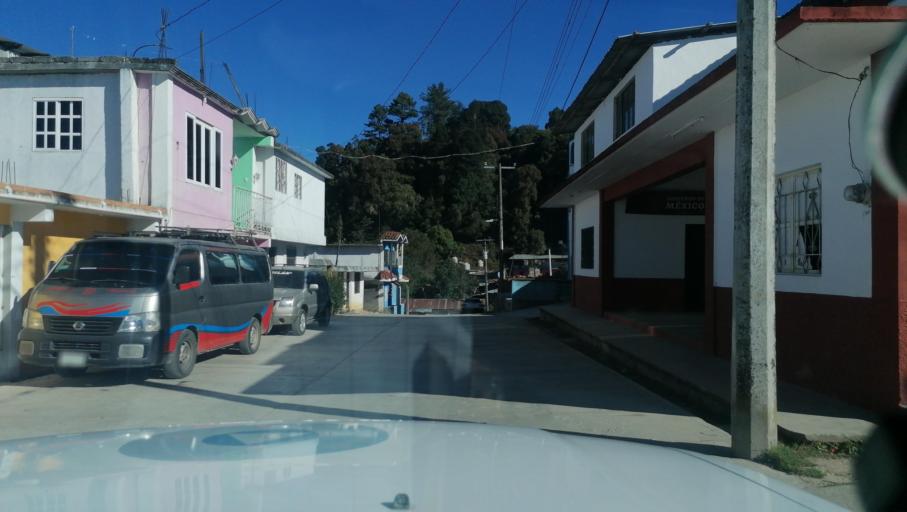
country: MX
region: Chiapas
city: Motozintla de Mendoza
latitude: 15.2593
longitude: -92.2136
